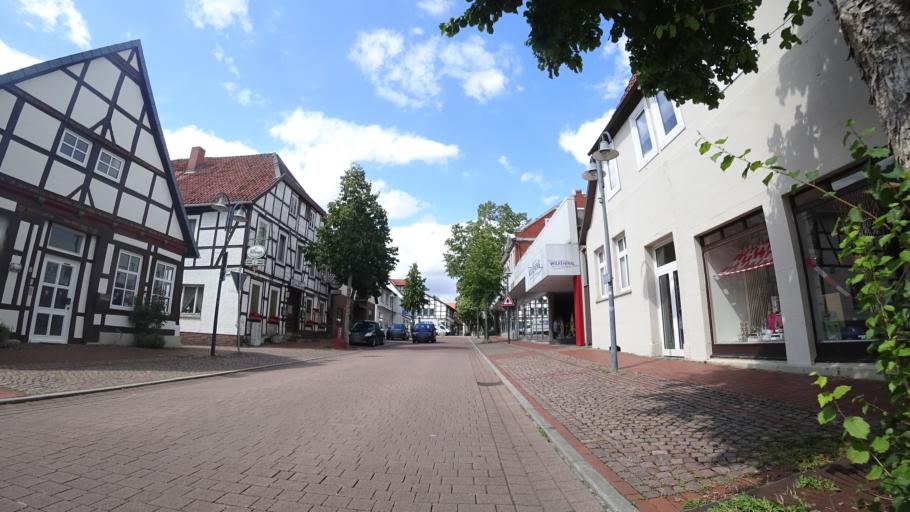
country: DE
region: North Rhine-Westphalia
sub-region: Regierungsbezirk Detmold
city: Petershagen
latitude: 52.3778
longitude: 8.9704
